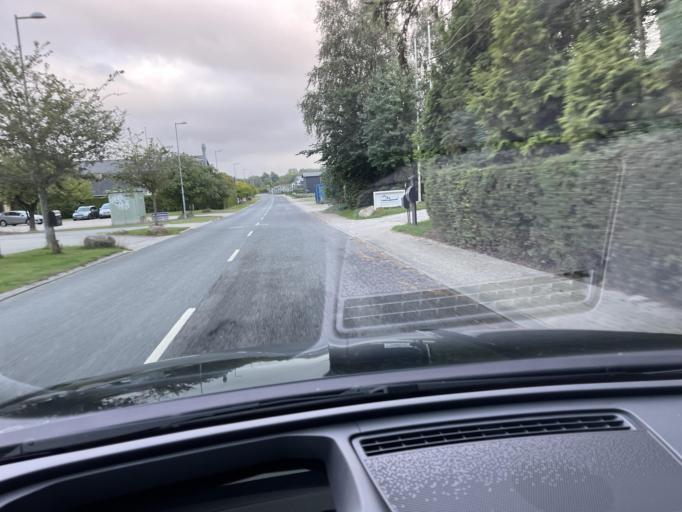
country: DK
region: Zealand
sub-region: Solrod Kommune
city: Havdrup
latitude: 55.5509
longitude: 12.1233
